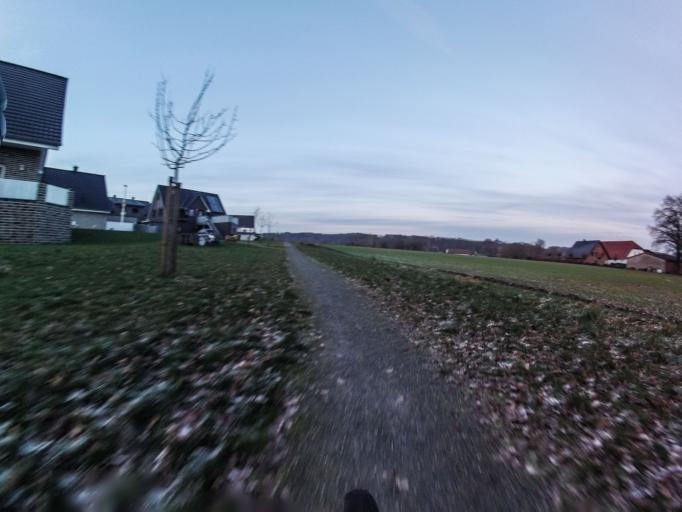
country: DE
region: North Rhine-Westphalia
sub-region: Regierungsbezirk Munster
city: Tecklenburg
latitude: 52.2625
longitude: 7.7950
